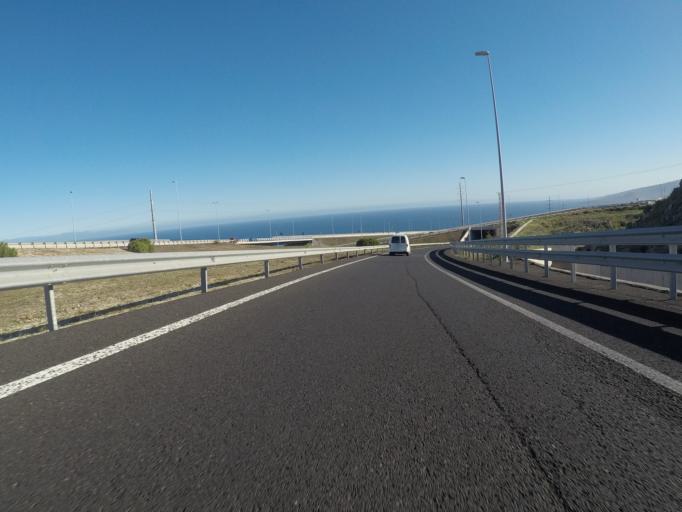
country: ES
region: Canary Islands
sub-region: Provincia de Santa Cruz de Tenerife
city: La Laguna
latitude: 28.4181
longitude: -16.3119
